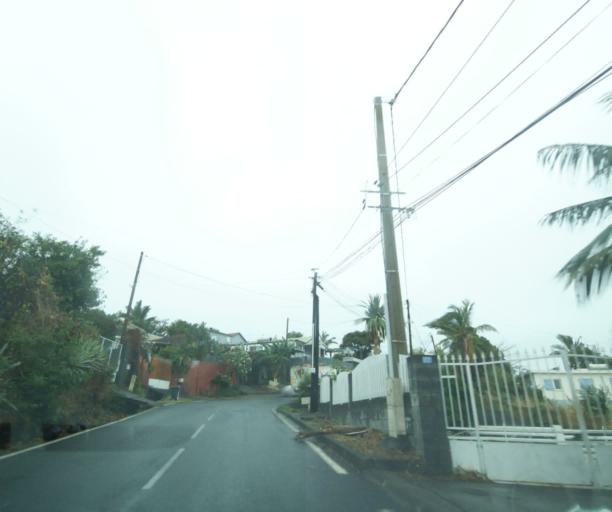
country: RE
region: Reunion
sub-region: Reunion
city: Saint-Paul
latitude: -21.0204
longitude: 55.2889
